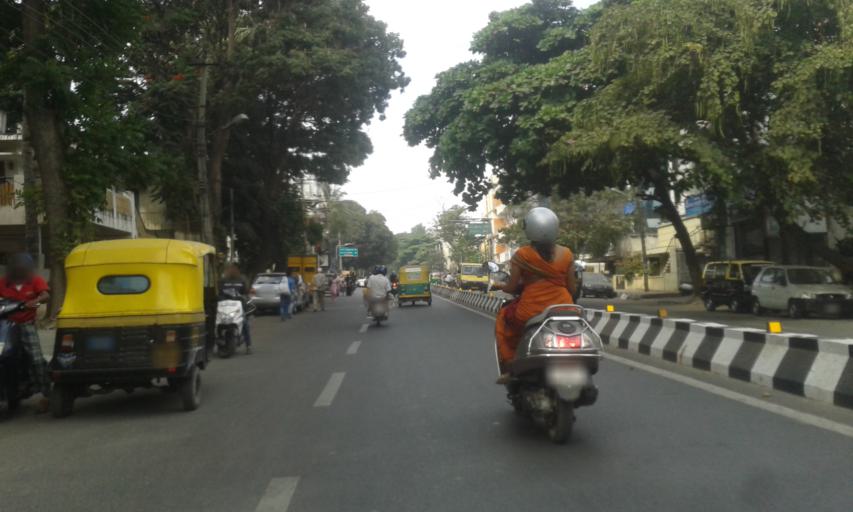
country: IN
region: Karnataka
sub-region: Bangalore Urban
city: Bangalore
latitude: 12.9284
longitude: 77.5981
